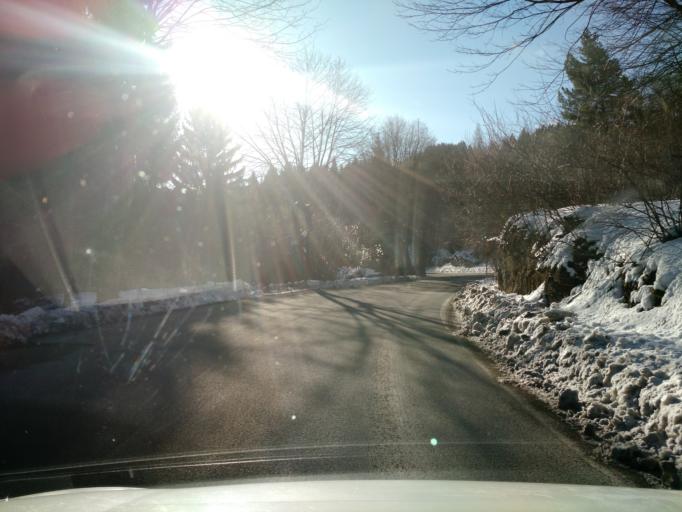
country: IT
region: Veneto
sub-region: Provincia di Vicenza
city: Roana
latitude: 45.8397
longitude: 11.4412
